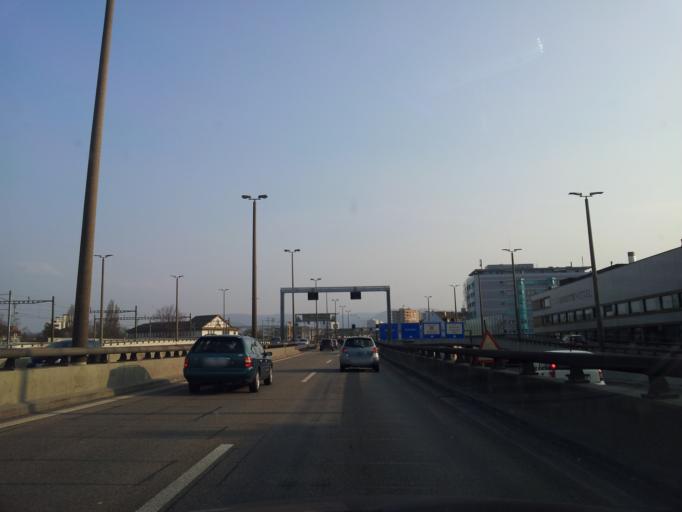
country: CH
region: Basel-Landschaft
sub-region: Bezirk Arlesheim
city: Birsfelden
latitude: 47.5570
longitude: 7.6145
